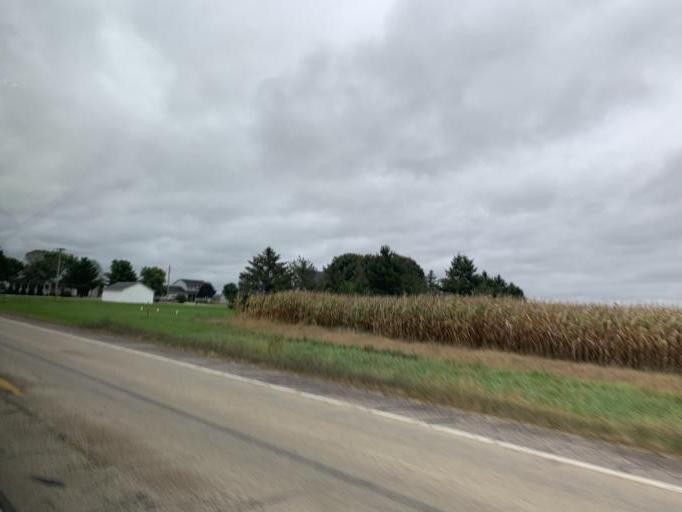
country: US
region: Wisconsin
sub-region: Sauk County
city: Sauk City
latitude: 43.2710
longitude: -89.7805
